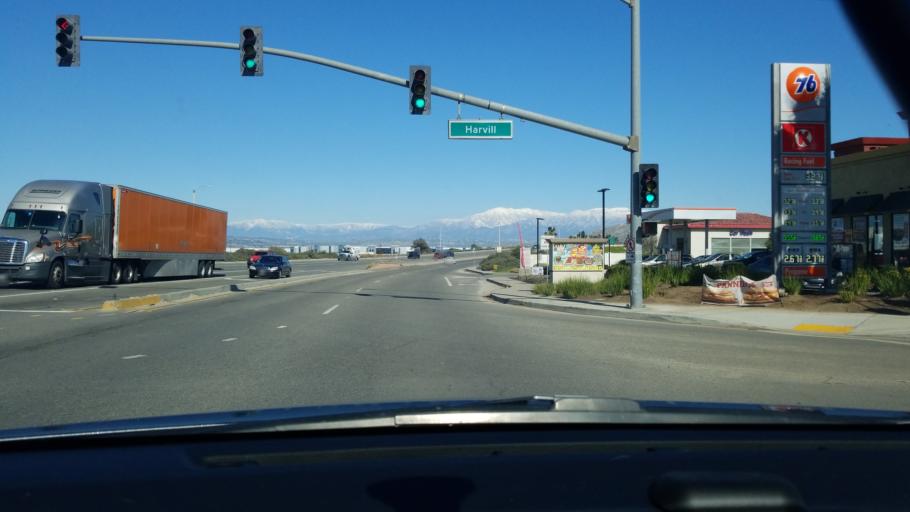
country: US
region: California
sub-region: Riverside County
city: Mead Valley
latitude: 33.8414
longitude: -117.2554
